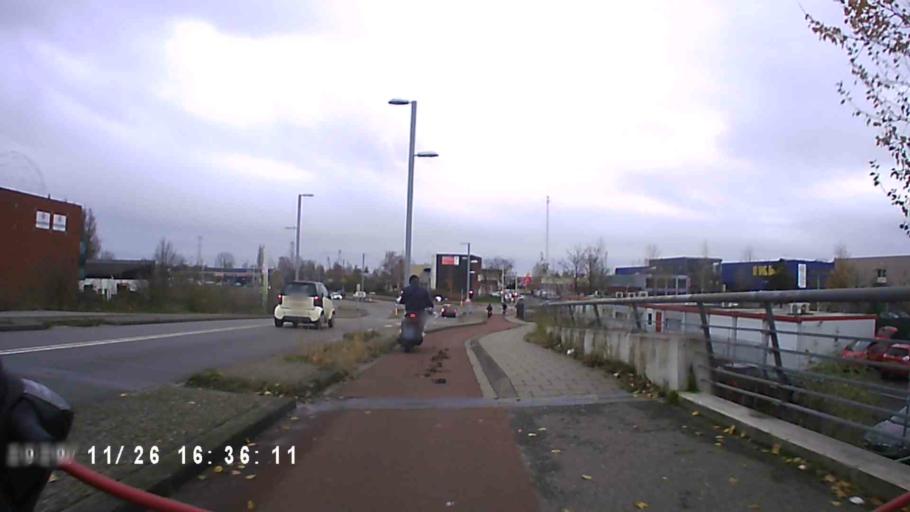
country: NL
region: Groningen
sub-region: Gemeente Groningen
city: Oosterpark
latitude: 53.2197
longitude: 6.5906
